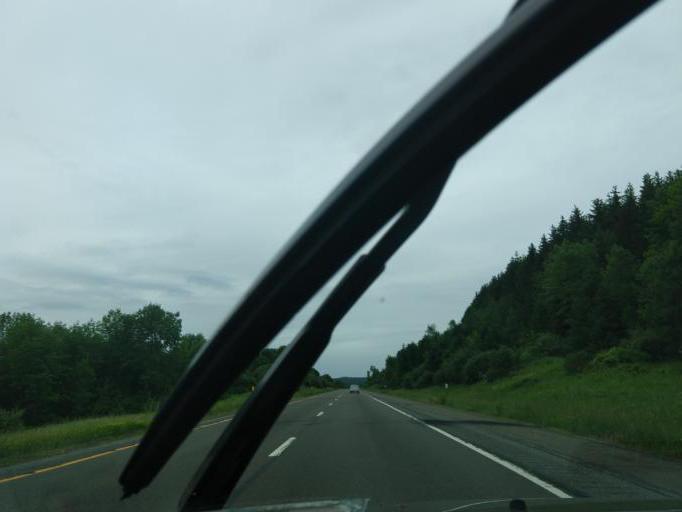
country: US
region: New York
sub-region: Broome County
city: Chenango Bridge
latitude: 42.2697
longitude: -75.9235
